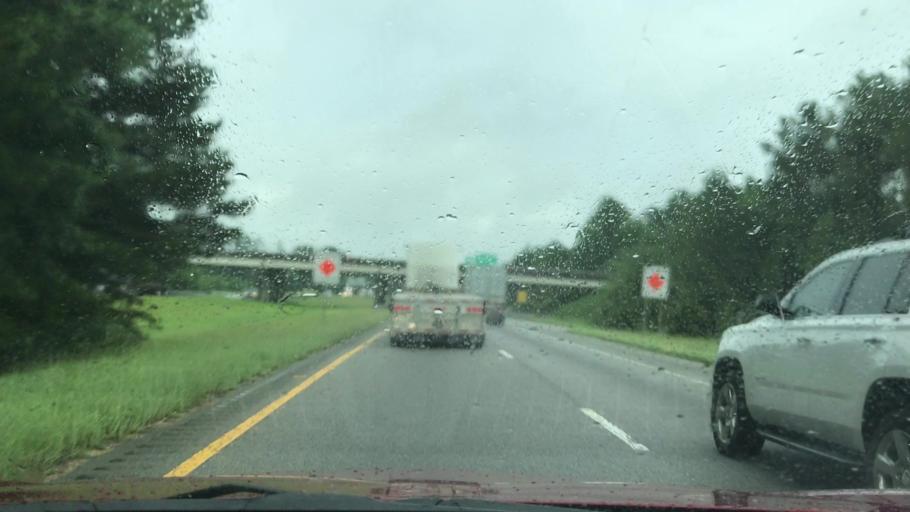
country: US
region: South Carolina
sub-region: Orangeburg County
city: Holly Hill
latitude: 33.2874
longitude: -80.5147
